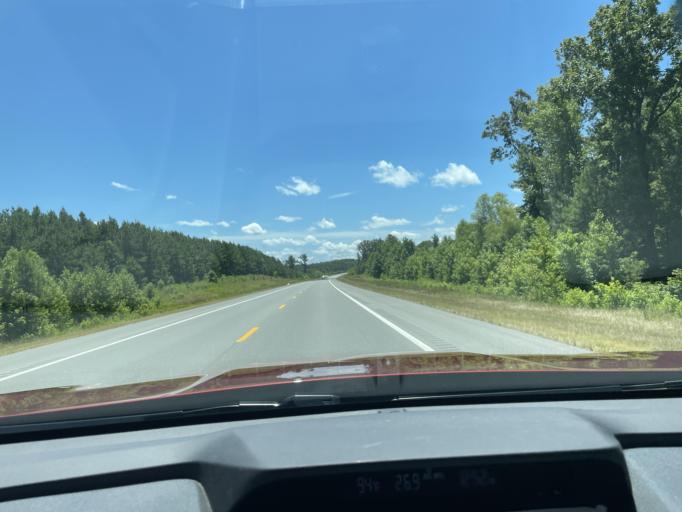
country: US
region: Arkansas
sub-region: Lincoln County
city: Star City
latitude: 33.9259
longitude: -91.8866
